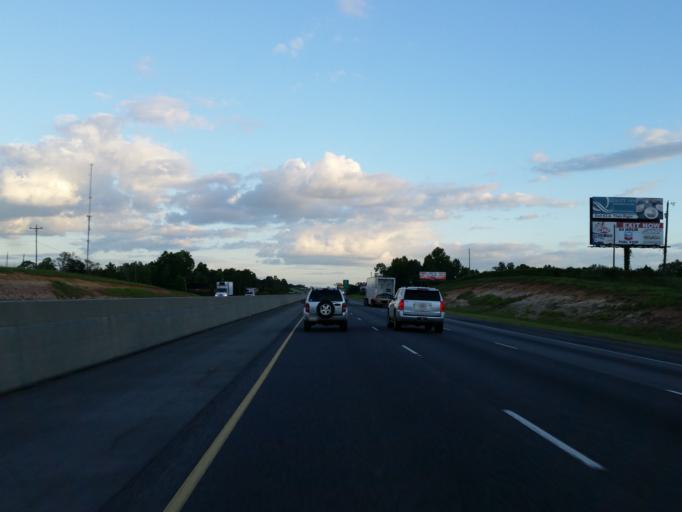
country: US
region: Georgia
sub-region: Turner County
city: Ashburn
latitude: 31.7466
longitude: -83.6601
